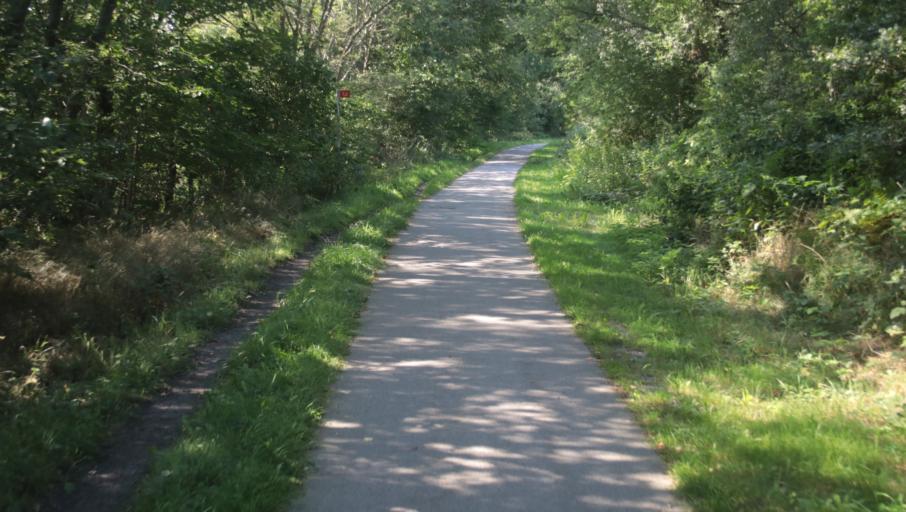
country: SE
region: Blekinge
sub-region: Karlshamns Kommun
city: Svangsta
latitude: 56.2431
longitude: 14.7968
